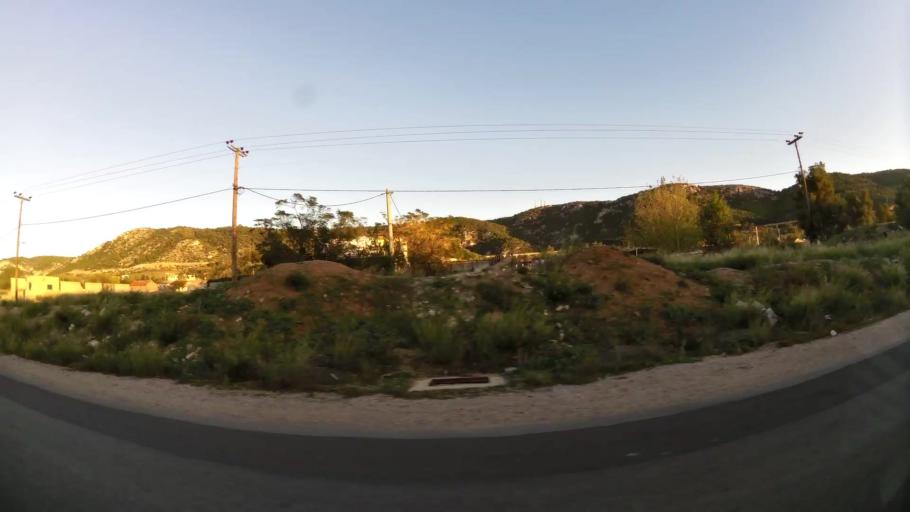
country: GR
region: Attica
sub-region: Nomarchia Athinas
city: Skaramangas
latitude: 38.0395
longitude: 23.6301
